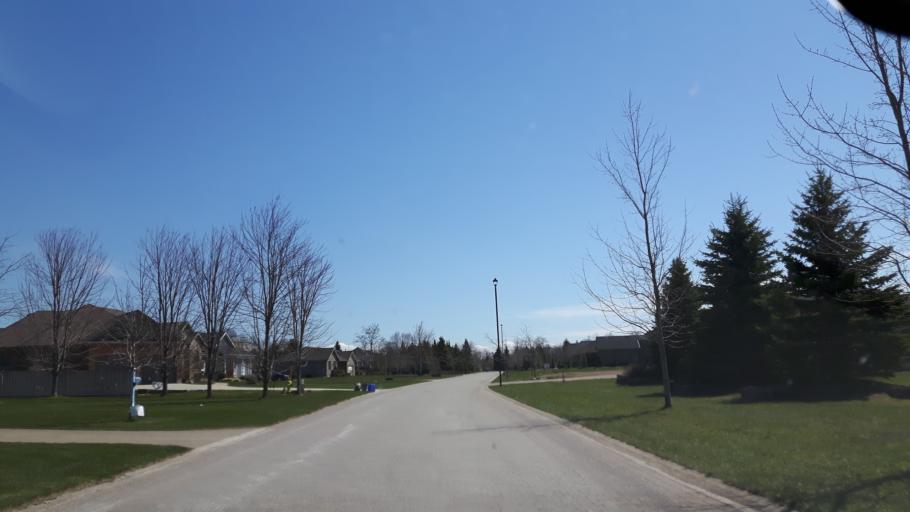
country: CA
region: Ontario
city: Bluewater
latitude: 43.5735
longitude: -81.6910
